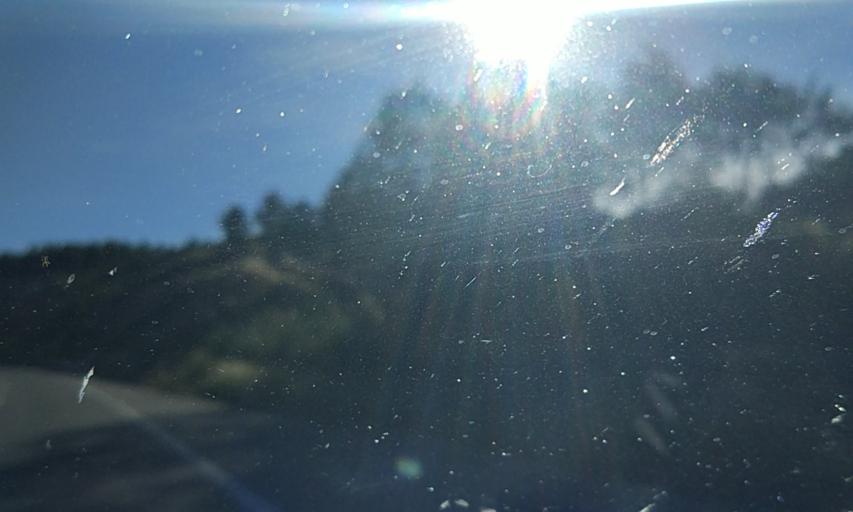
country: PT
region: Vila Real
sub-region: Murca
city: Murca
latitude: 41.3971
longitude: -7.4713
